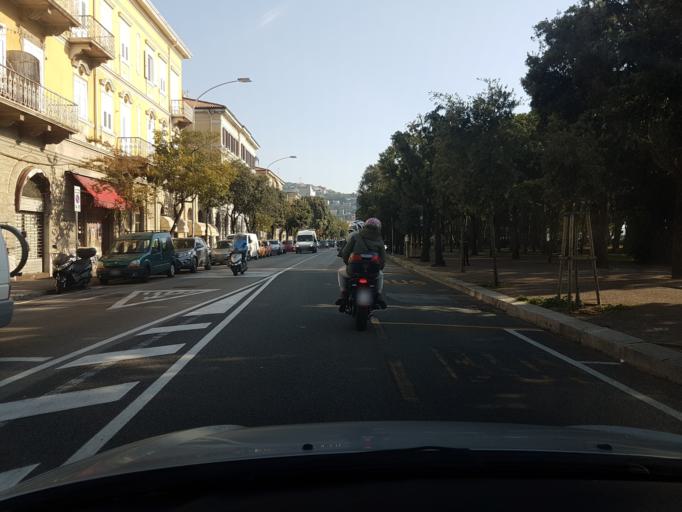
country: IT
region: Friuli Venezia Giulia
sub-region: Provincia di Trieste
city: Prosecco-Contovello
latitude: 45.6849
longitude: 13.7492
